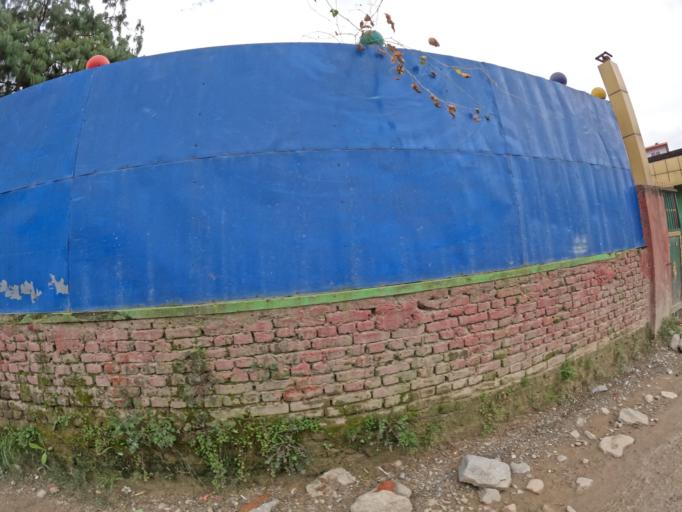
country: NP
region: Central Region
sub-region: Bagmati Zone
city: Kathmandu
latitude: 27.7413
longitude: 85.3135
